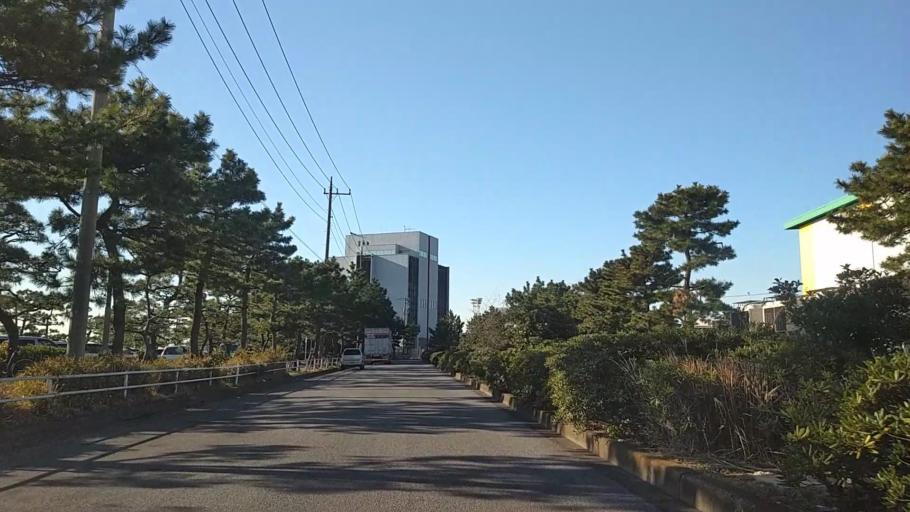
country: JP
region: Kanagawa
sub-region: Kawasaki-shi
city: Kawasaki
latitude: 35.6084
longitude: 139.7913
